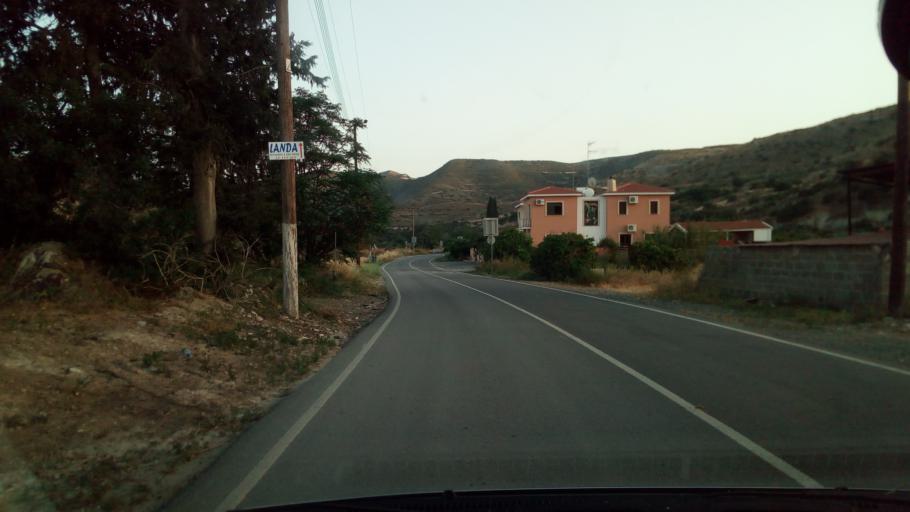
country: CY
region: Larnaka
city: Kofinou
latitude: 34.7939
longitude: 33.3847
